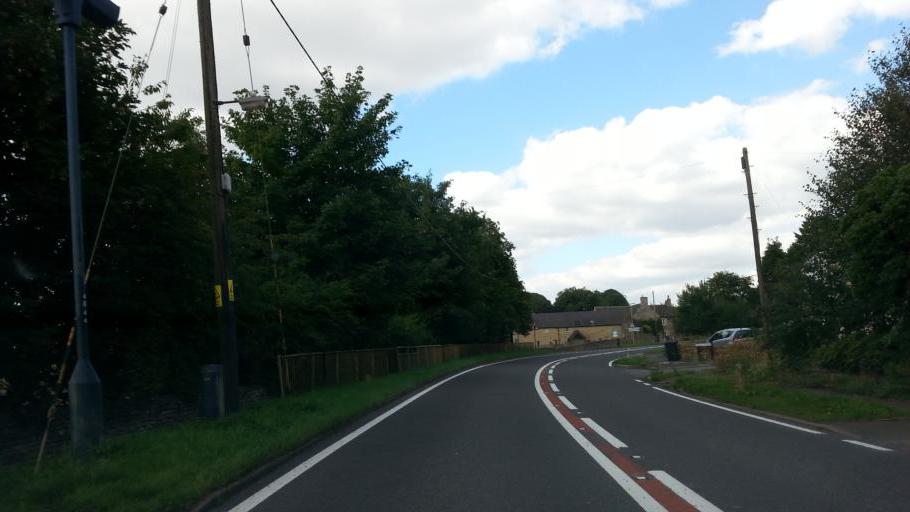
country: GB
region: England
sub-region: District of Rutland
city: Ketton
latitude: 52.6122
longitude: -0.5314
